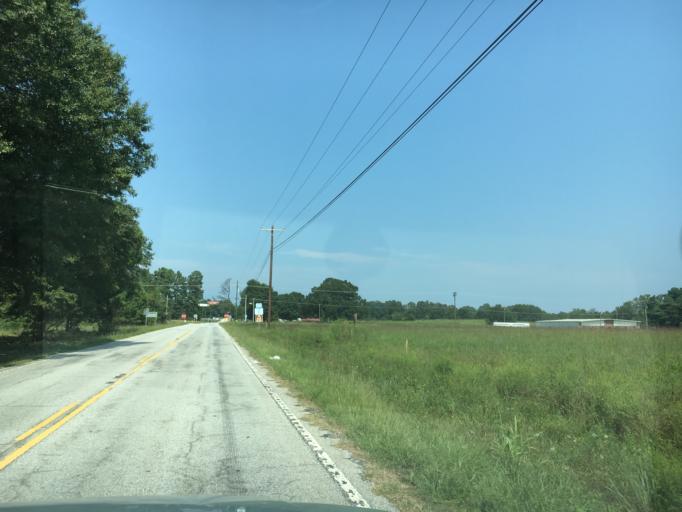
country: US
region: South Carolina
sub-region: Spartanburg County
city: Mayo
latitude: 35.1579
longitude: -81.9178
